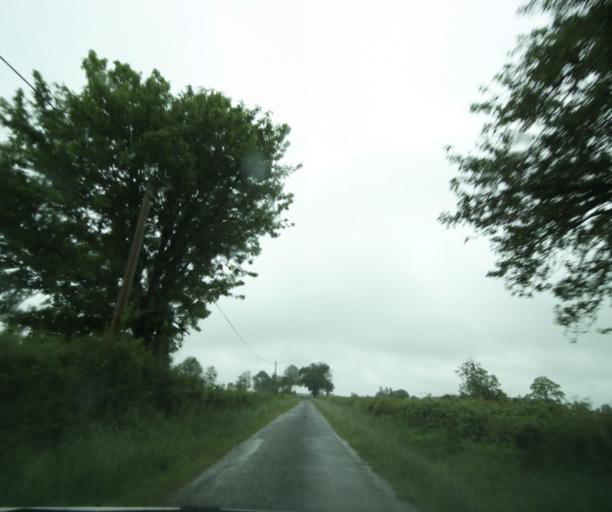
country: FR
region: Bourgogne
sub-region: Departement de Saone-et-Loire
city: Ciry-le-Noble
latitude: 46.5604
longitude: 4.3258
